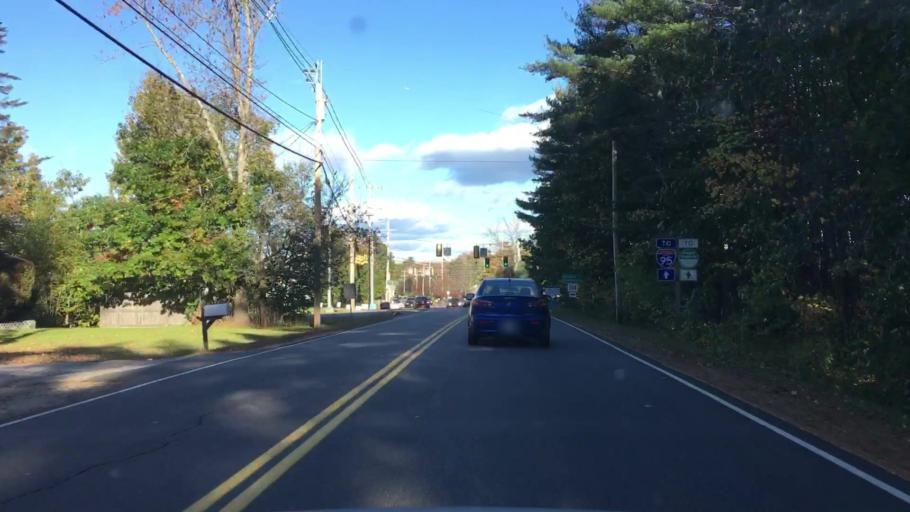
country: US
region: Maine
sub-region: Cumberland County
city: South Portland Gardens
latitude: 43.6185
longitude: -70.3470
